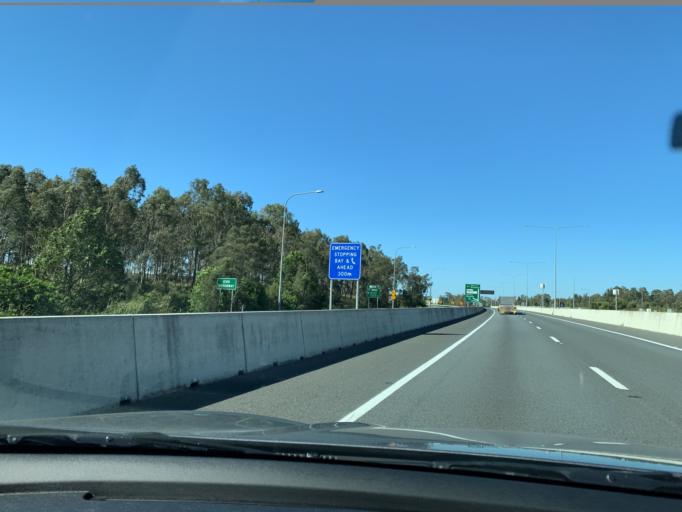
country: AU
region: Queensland
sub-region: Brisbane
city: Wynnum
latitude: -27.4398
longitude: 153.1374
